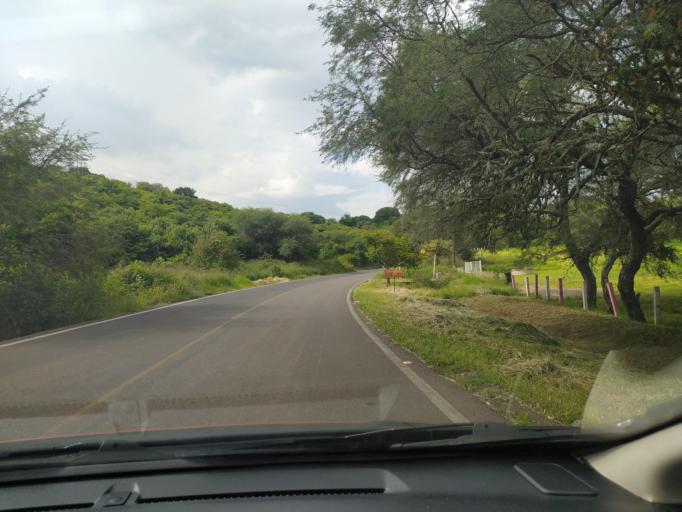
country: MX
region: Jalisco
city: Villa Corona
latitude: 20.4069
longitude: -103.6846
